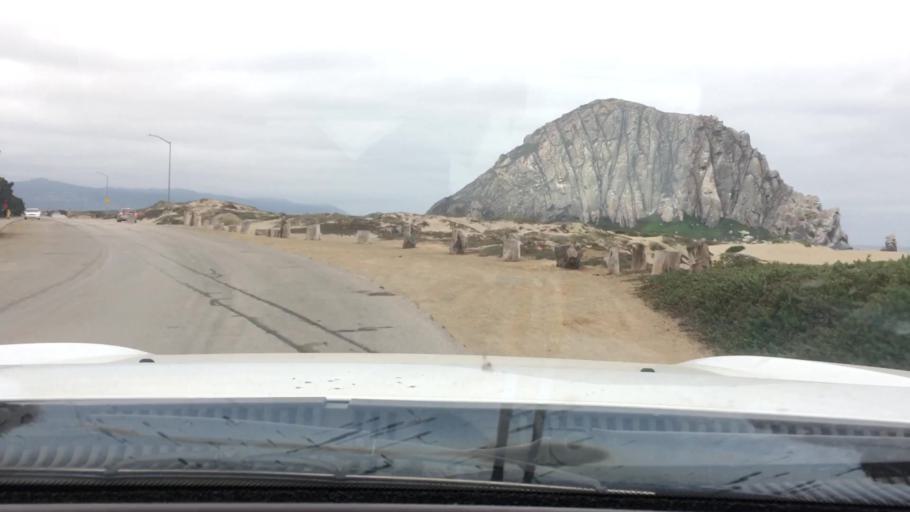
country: US
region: California
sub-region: San Luis Obispo County
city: Morro Bay
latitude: 35.3790
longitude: -120.8621
